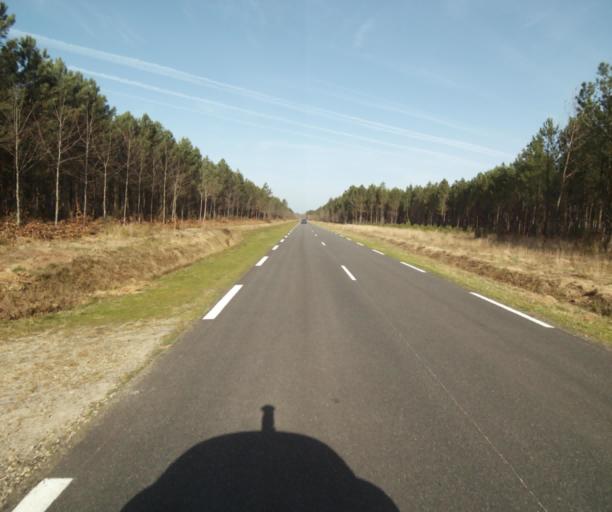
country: FR
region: Aquitaine
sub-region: Departement de la Gironde
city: Grignols
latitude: 44.1876
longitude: -0.1058
